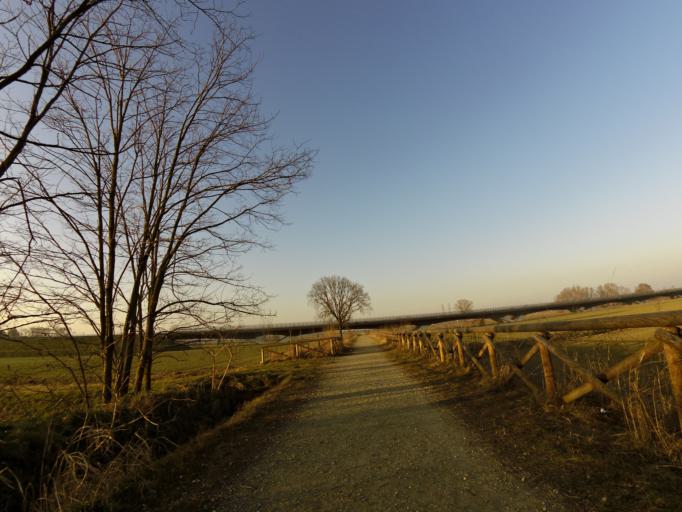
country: IT
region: Lombardy
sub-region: Citta metropolitana di Milano
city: Melegnano
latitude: 45.3670
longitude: 9.3287
